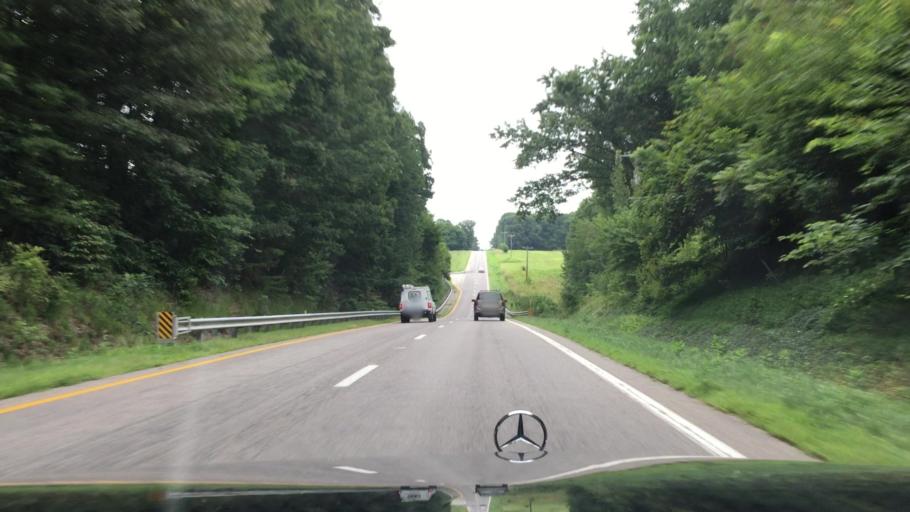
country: US
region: Virginia
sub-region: Prince Edward County
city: Hampden Sydney
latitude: 37.3060
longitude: -78.5189
